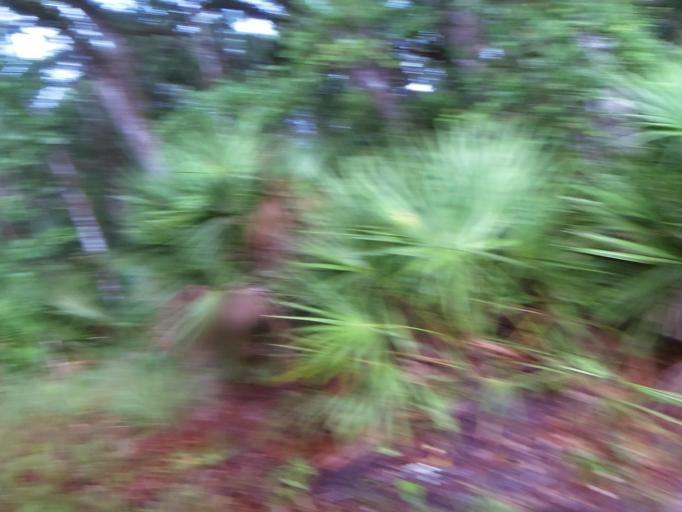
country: US
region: Florida
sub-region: Putnam County
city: Palatka
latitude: 29.6771
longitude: -81.7521
